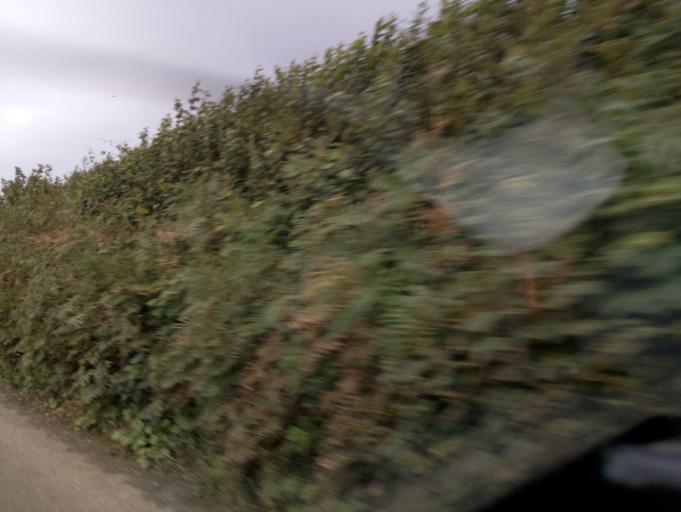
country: GB
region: England
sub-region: Devon
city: Kingsbridge
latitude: 50.2940
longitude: -3.7873
